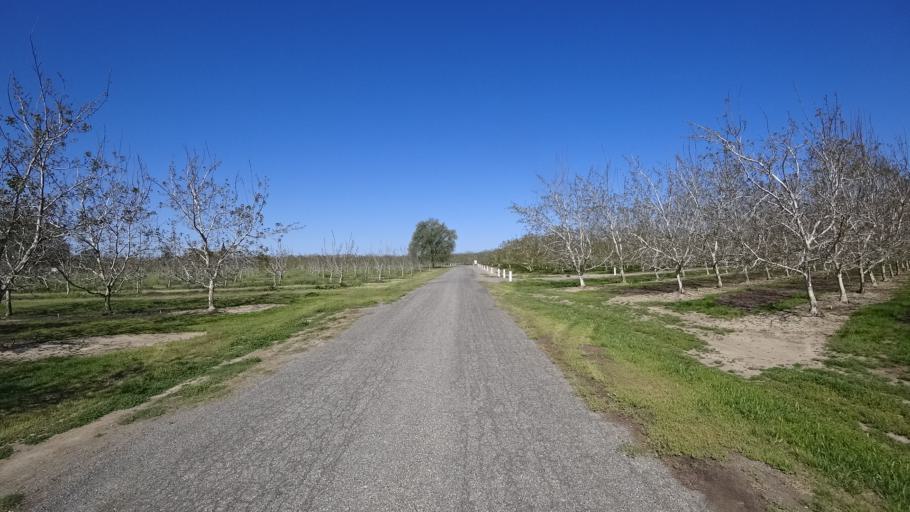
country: US
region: California
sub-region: Glenn County
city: Hamilton City
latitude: 39.7219
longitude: -122.0235
